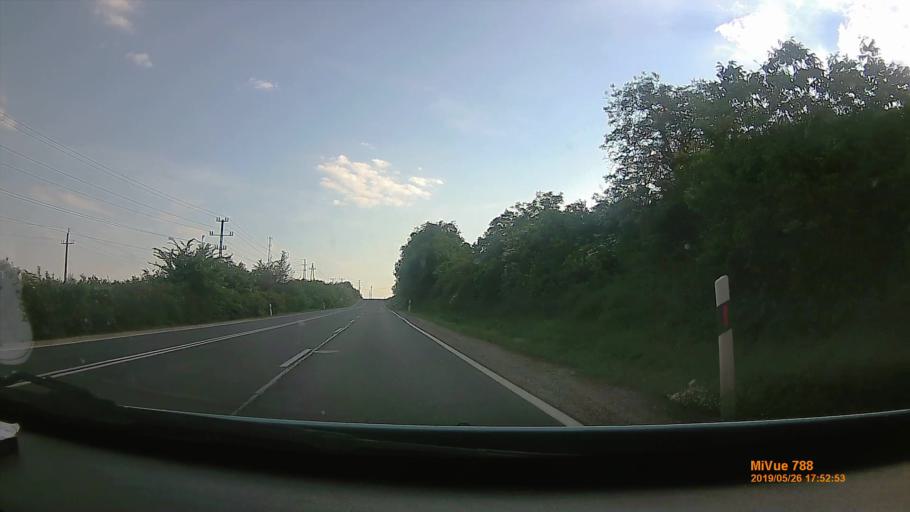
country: HU
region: Borsod-Abauj-Zemplen
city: Onga
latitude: 48.1591
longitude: 20.9023
